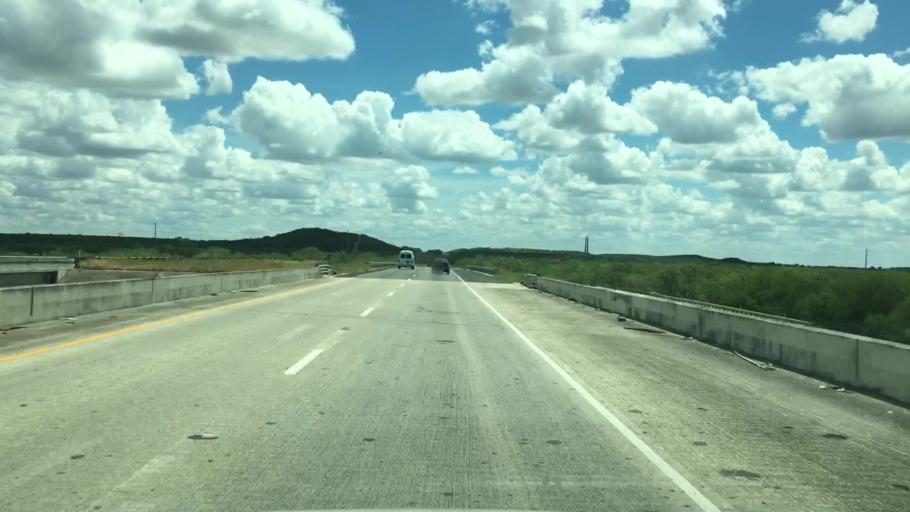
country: US
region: Texas
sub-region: Live Oak County
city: Three Rivers
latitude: 28.7335
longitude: -98.2893
